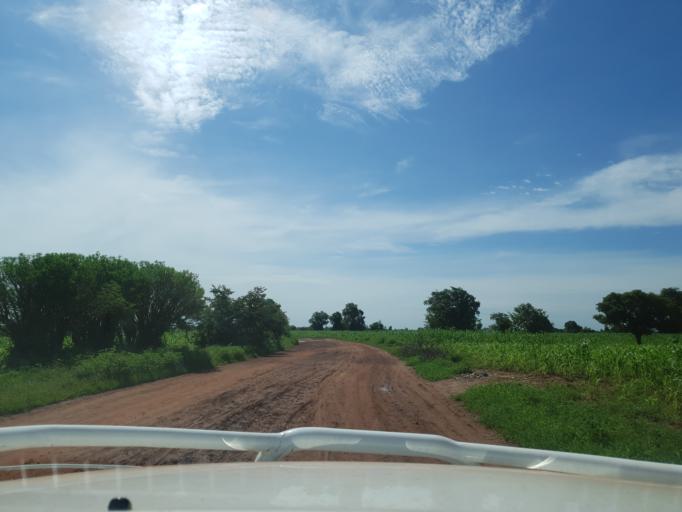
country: ML
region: Koulikoro
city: Banamba
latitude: 13.2765
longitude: -7.5469
